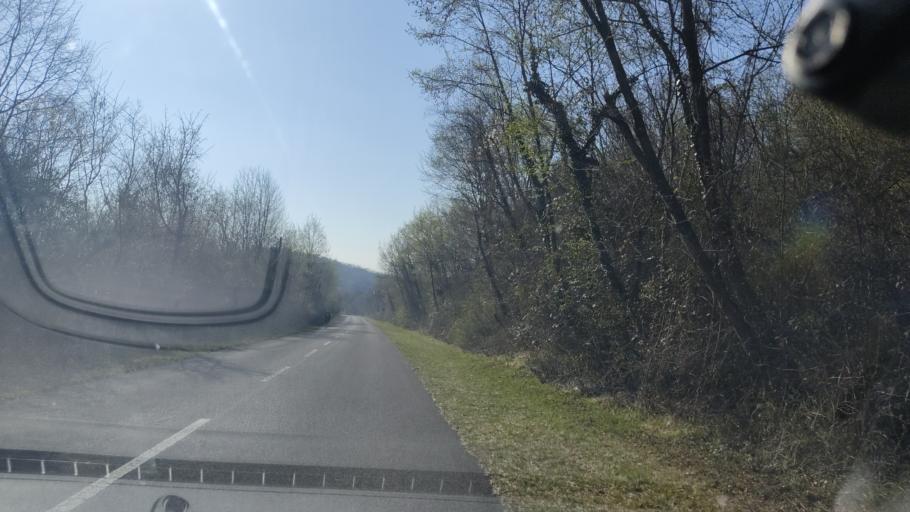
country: IT
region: Friuli Venezia Giulia
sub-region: Provincia di Pordenone
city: Budoia
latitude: 46.0625
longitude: 12.5171
